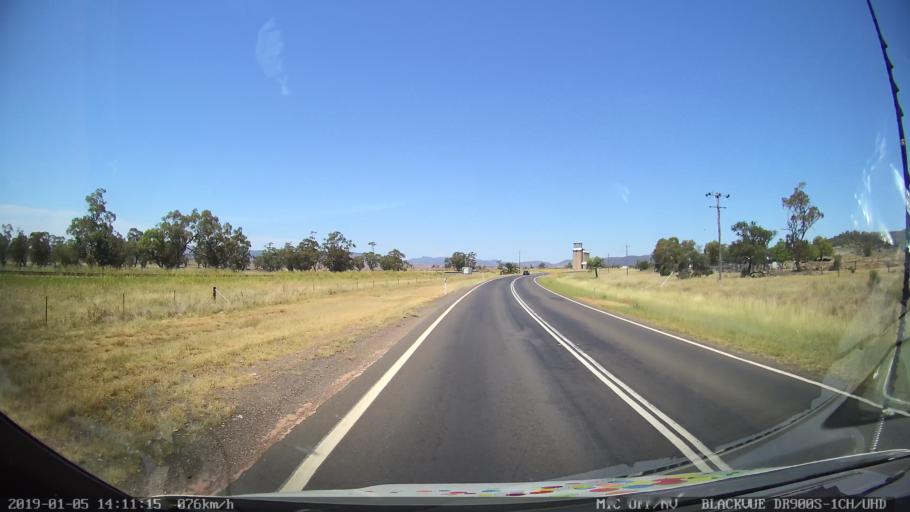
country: AU
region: New South Wales
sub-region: Gunnedah
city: Gunnedah
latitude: -31.2440
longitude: 150.4557
